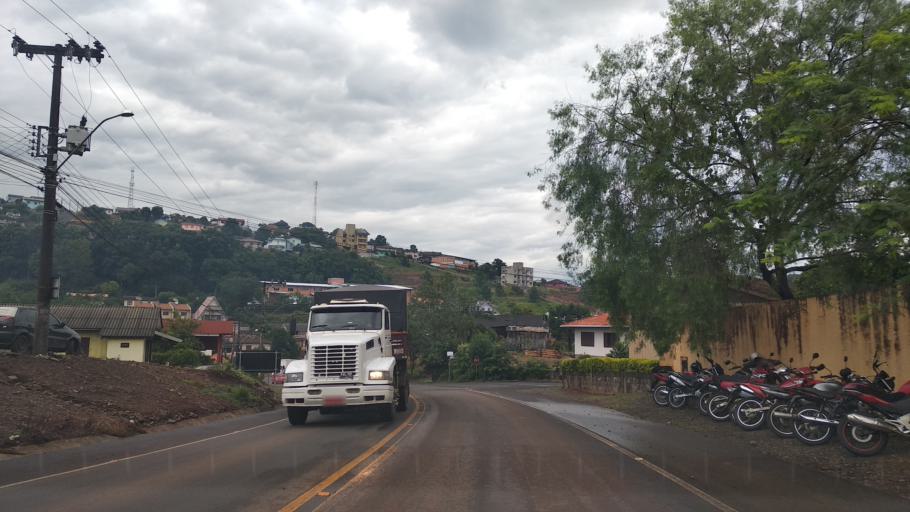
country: BR
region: Santa Catarina
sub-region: Videira
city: Videira
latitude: -27.0944
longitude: -51.2459
